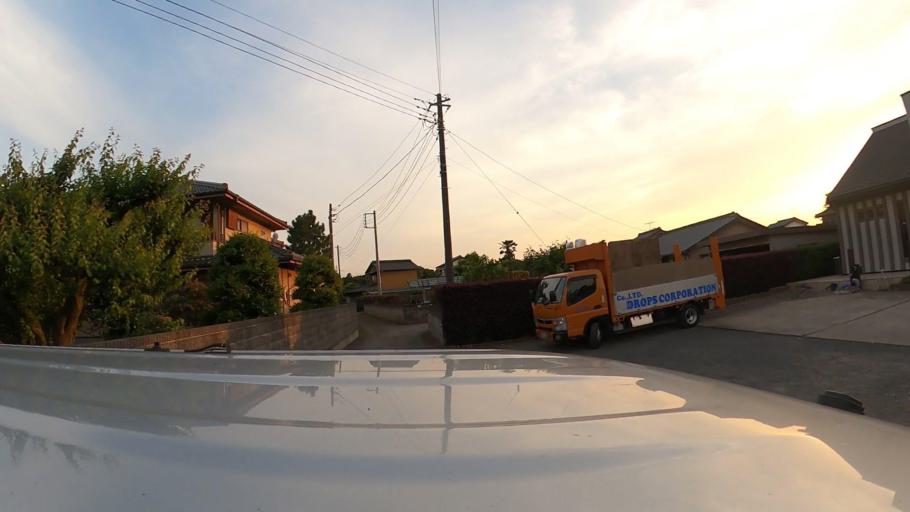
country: JP
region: Ibaraki
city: Ushiku
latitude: 36.0232
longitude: 140.0948
